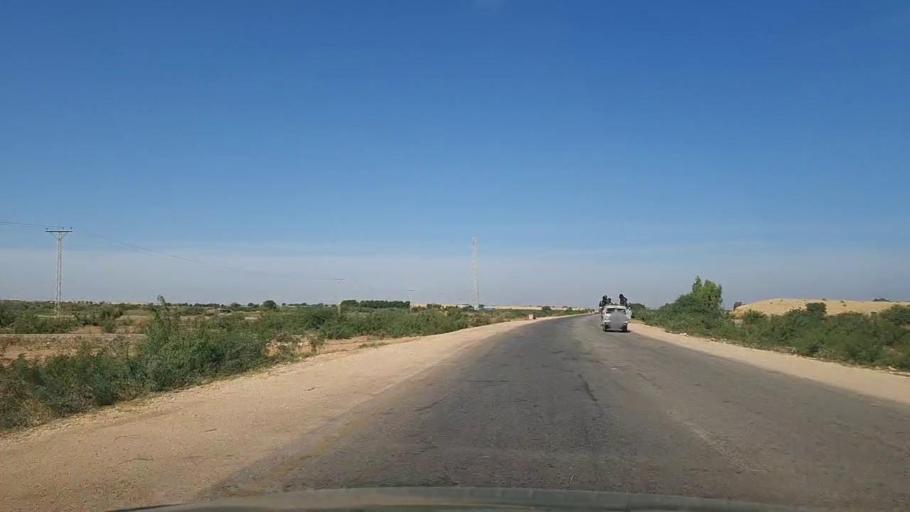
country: PK
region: Sindh
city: Kotri
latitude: 25.2016
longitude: 68.2375
